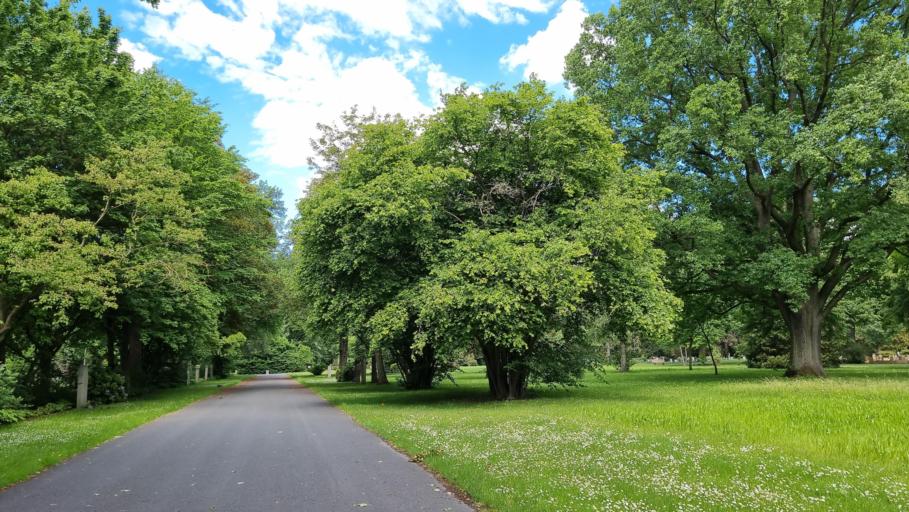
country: DE
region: Lower Saxony
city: Auf der Horst
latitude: 52.4057
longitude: 9.6715
